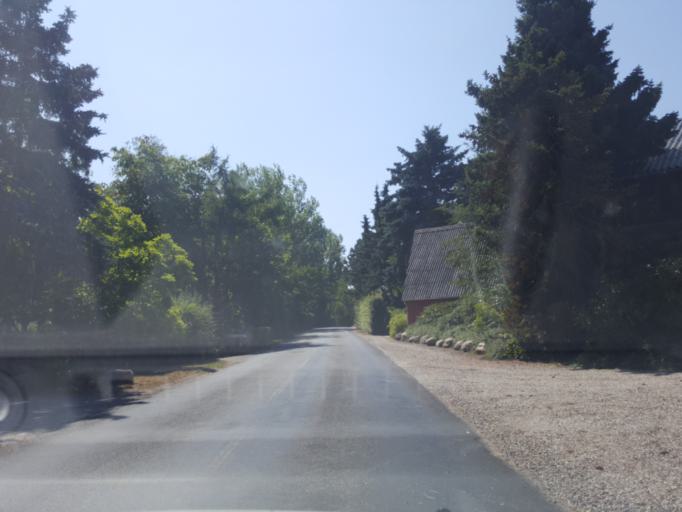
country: DK
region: Capital Region
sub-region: Fredensborg Kommune
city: Kokkedal
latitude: 55.9267
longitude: 12.4628
